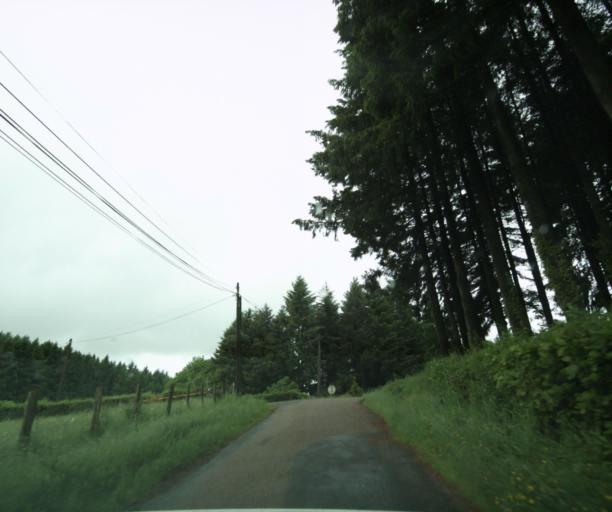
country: FR
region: Bourgogne
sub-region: Departement de Saone-et-Loire
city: Matour
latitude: 46.4363
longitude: 4.4633
